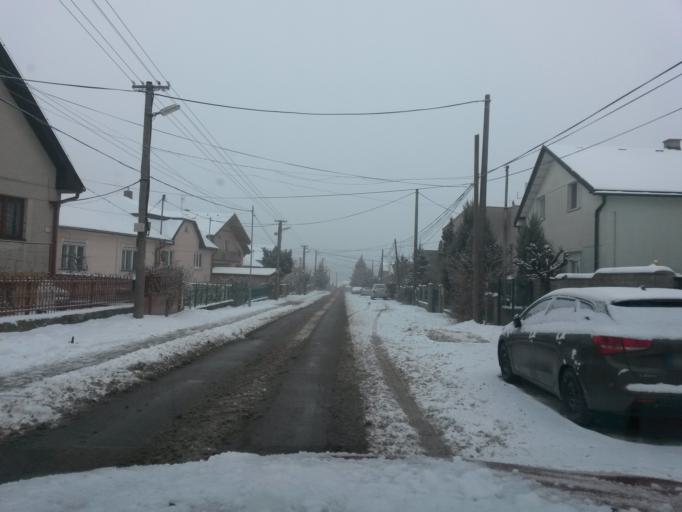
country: SK
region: Kosicky
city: Kosice
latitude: 48.7305
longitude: 21.3017
